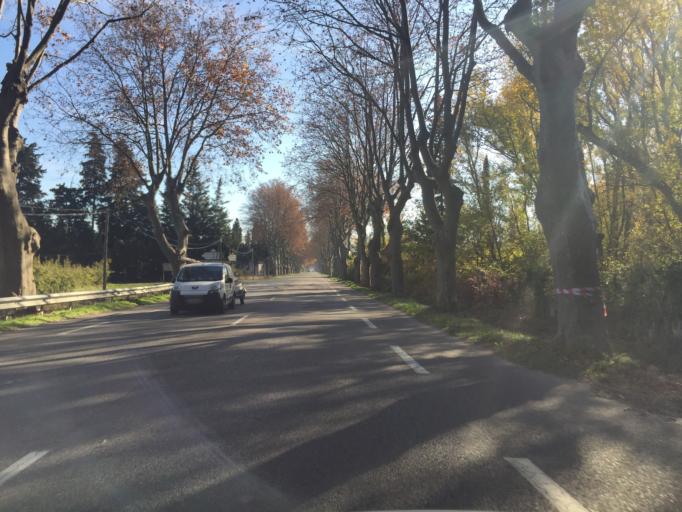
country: FR
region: Provence-Alpes-Cote d'Azur
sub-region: Departement des Bouches-du-Rhone
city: Orgon
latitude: 43.7804
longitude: 5.0513
